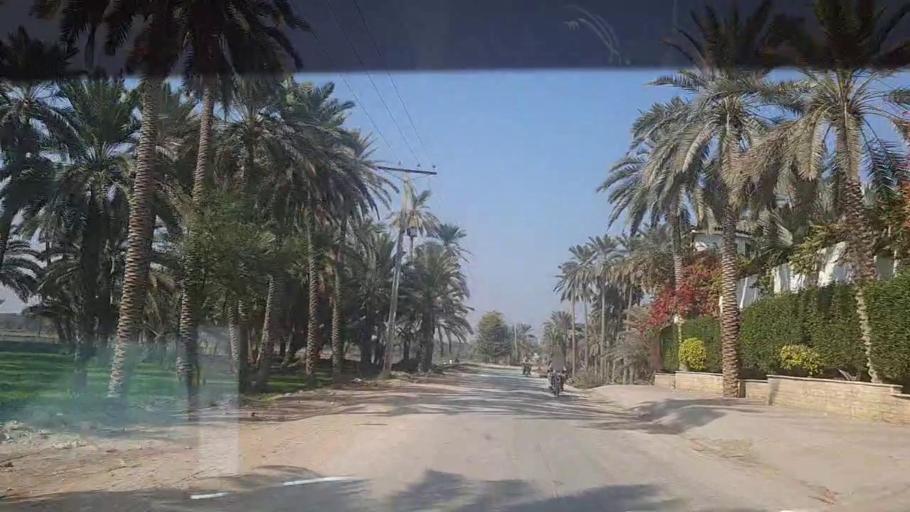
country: PK
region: Sindh
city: Kot Diji
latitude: 27.3804
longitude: 68.6901
